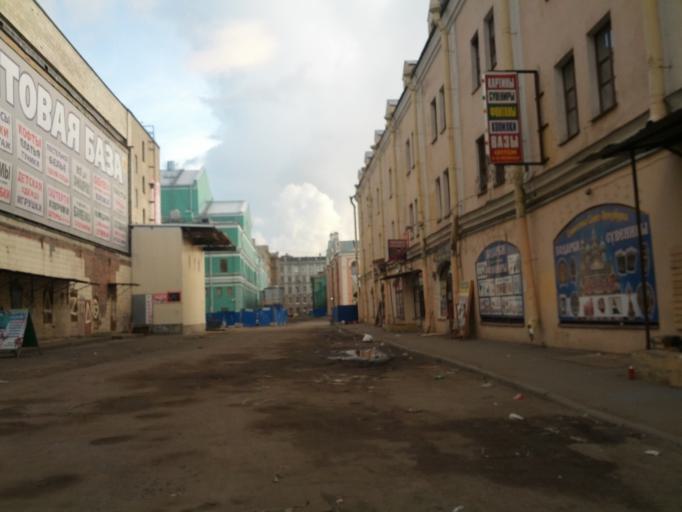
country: RU
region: St.-Petersburg
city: Saint Petersburg
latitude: 59.9288
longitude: 30.3317
